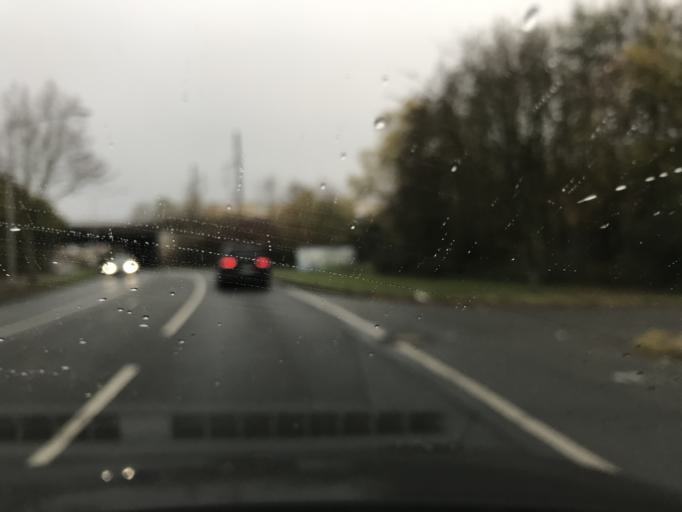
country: DE
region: North Rhine-Westphalia
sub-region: Regierungsbezirk Arnsberg
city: Hamm
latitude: 51.6992
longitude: 7.8208
